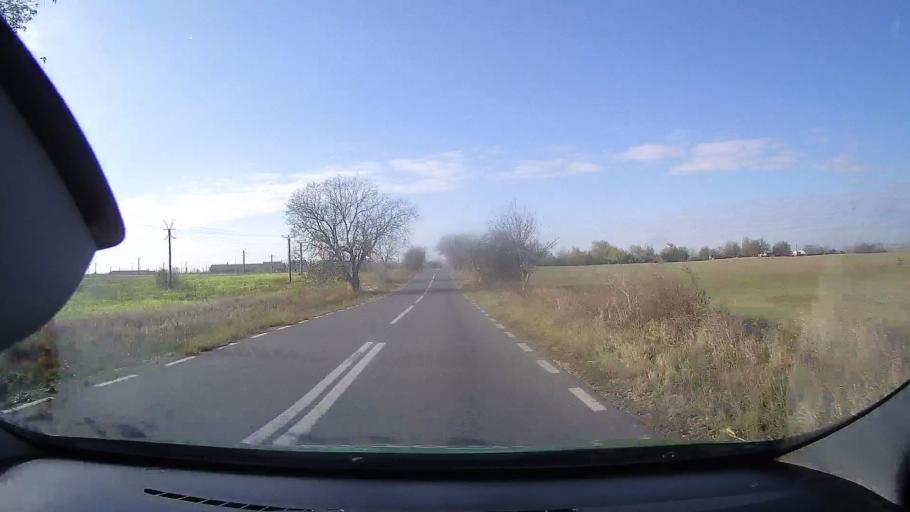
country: RO
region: Tulcea
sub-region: Comuna Murighiol
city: Murighiol
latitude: 45.0262
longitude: 29.1366
